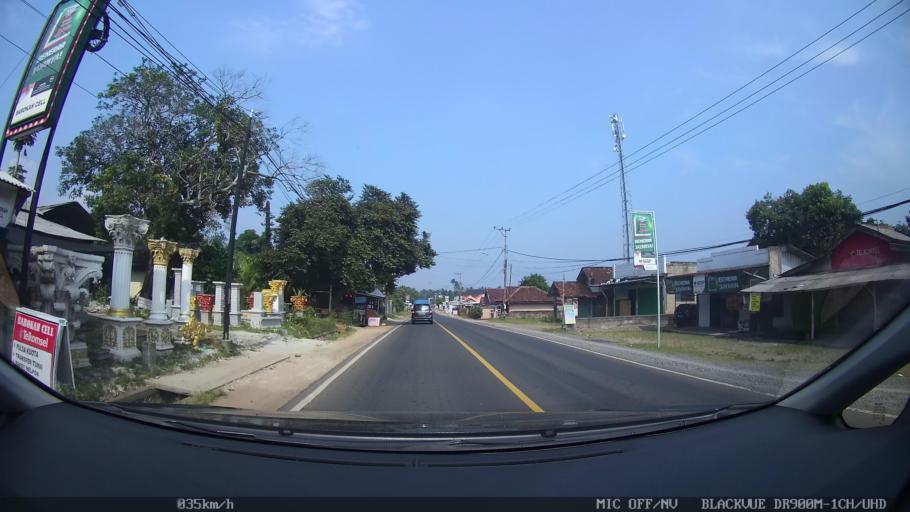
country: ID
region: Lampung
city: Gedongtataan
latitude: -5.3659
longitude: 105.1501
